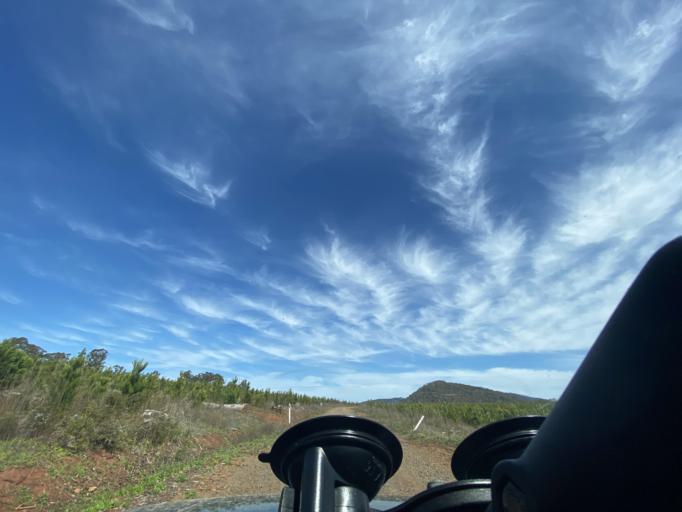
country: AU
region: Victoria
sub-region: Mansfield
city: Mansfield
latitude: -36.8230
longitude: 146.1034
